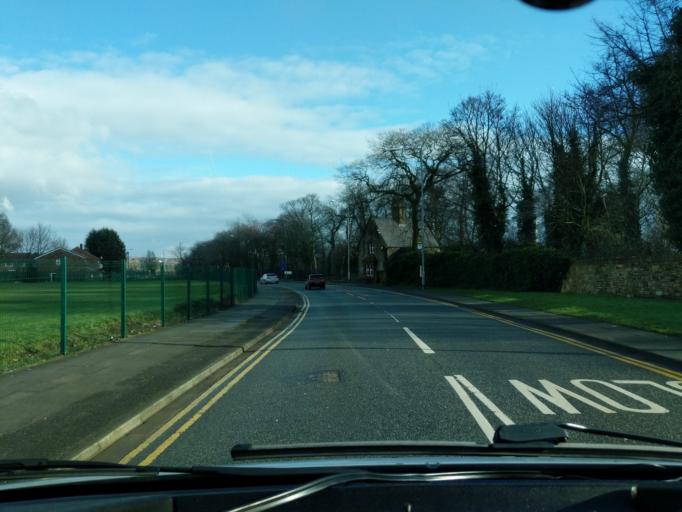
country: GB
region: England
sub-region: St. Helens
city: St Helens
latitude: 53.4666
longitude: -2.7523
